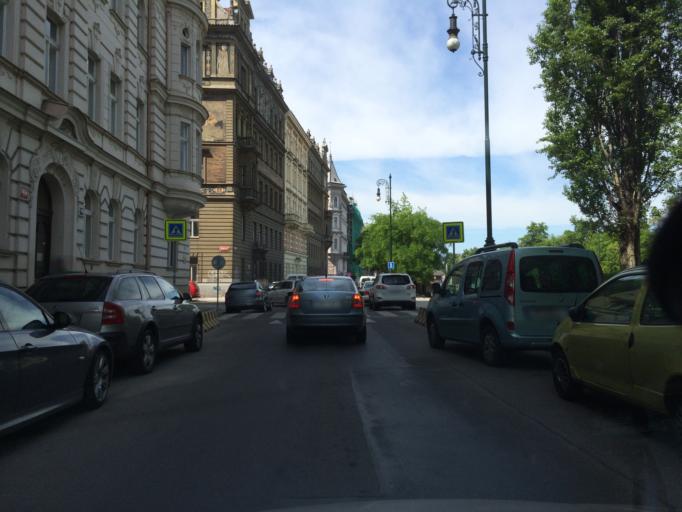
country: CZ
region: Praha
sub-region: Praha 1
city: Mala Strana
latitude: 50.0768
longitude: 14.4084
